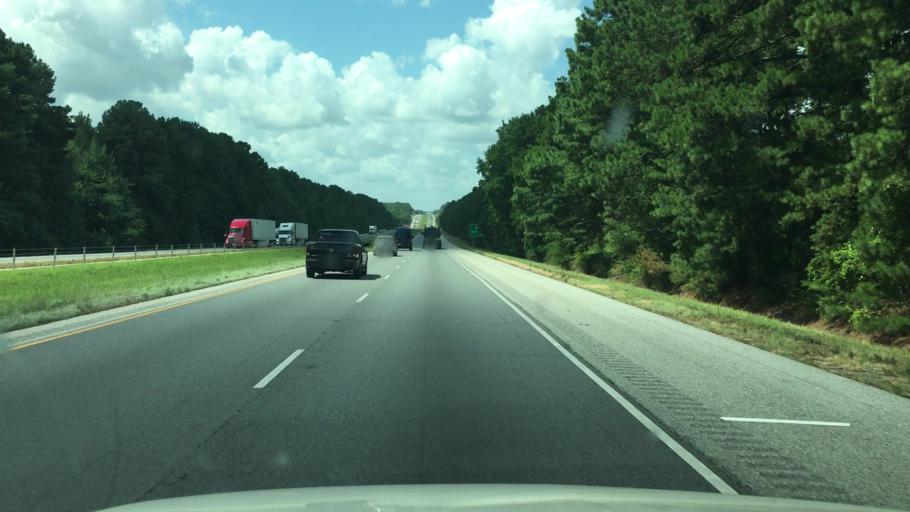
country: US
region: Arkansas
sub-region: Clark County
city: Arkadelphia
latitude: 34.0906
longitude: -93.1096
